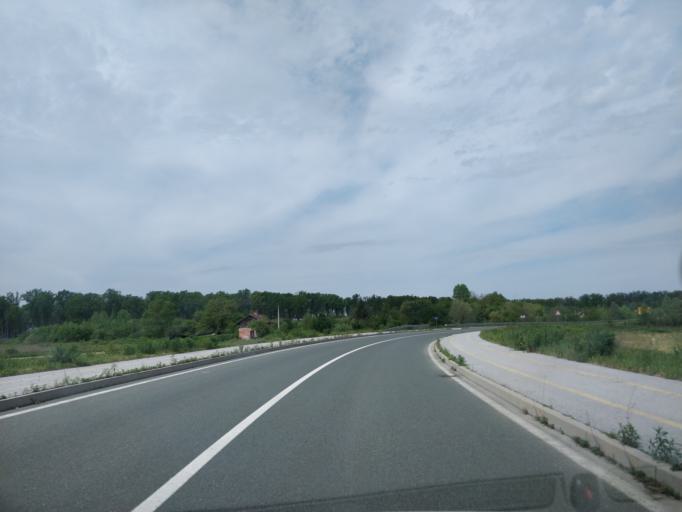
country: HR
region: Zagrebacka
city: Mraclin
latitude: 45.6231
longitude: 16.1058
